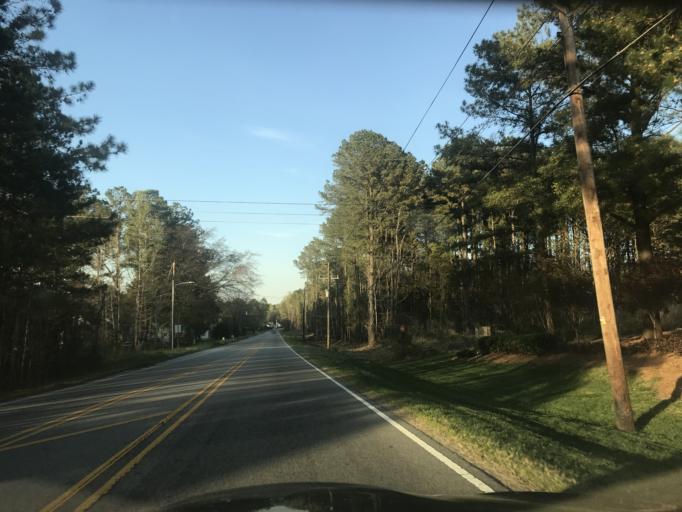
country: US
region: North Carolina
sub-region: Wake County
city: Knightdale
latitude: 35.7414
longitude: -78.5416
